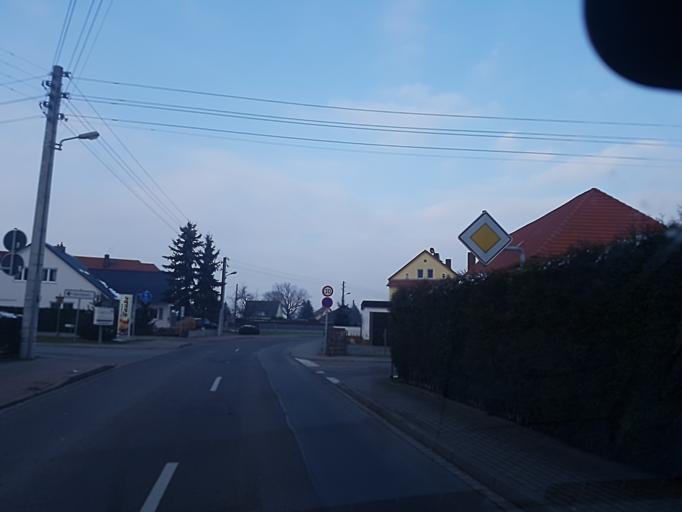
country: DE
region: Saxony
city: Oschatz
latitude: 51.3190
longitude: 13.0839
